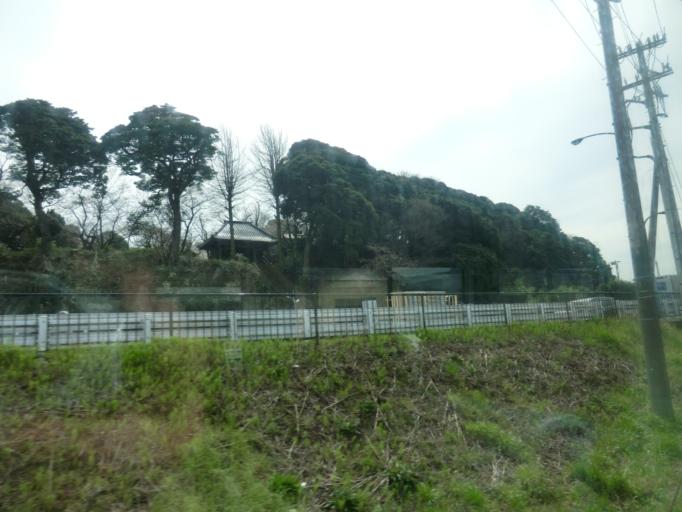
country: JP
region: Chiba
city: Kisarazu
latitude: 35.3641
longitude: 139.9227
